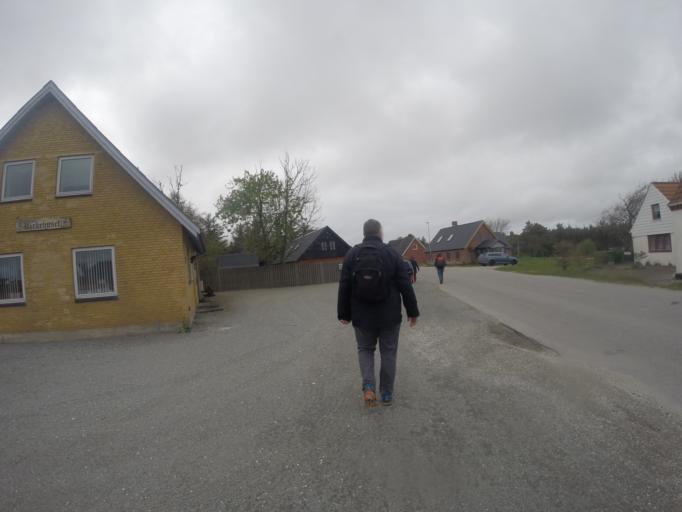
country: DK
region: North Denmark
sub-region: Thisted Kommune
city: Hurup
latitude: 56.9216
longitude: 8.3581
